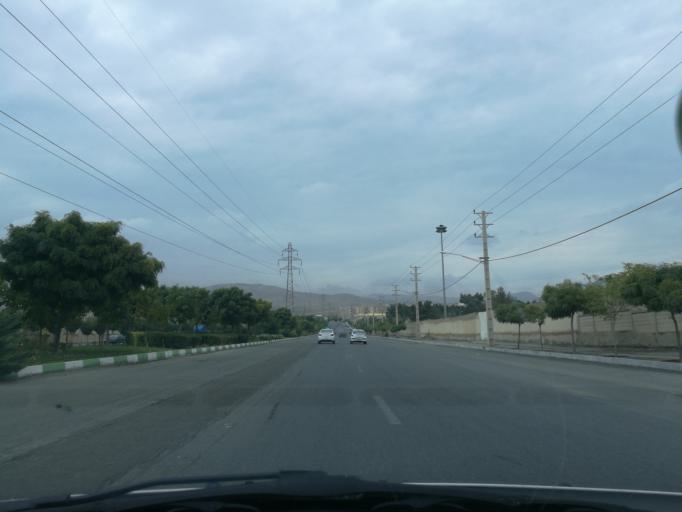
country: IR
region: Alborz
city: Karaj
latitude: 35.8584
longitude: 50.9230
